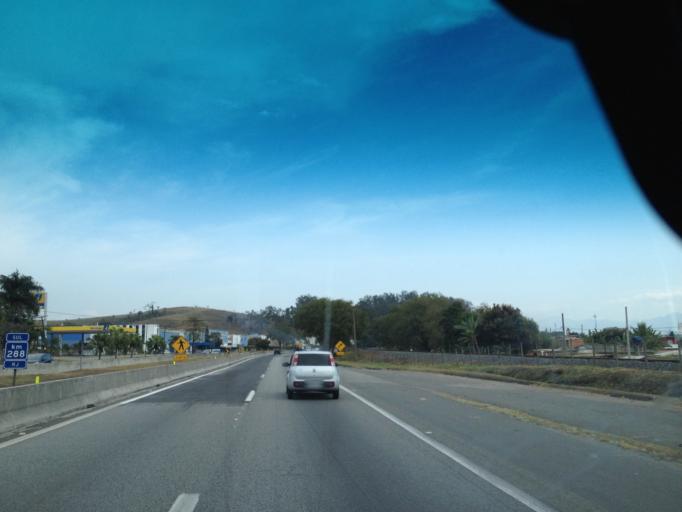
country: BR
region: Rio de Janeiro
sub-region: Porto Real
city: Porto Real
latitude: -22.4642
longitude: -44.2860
